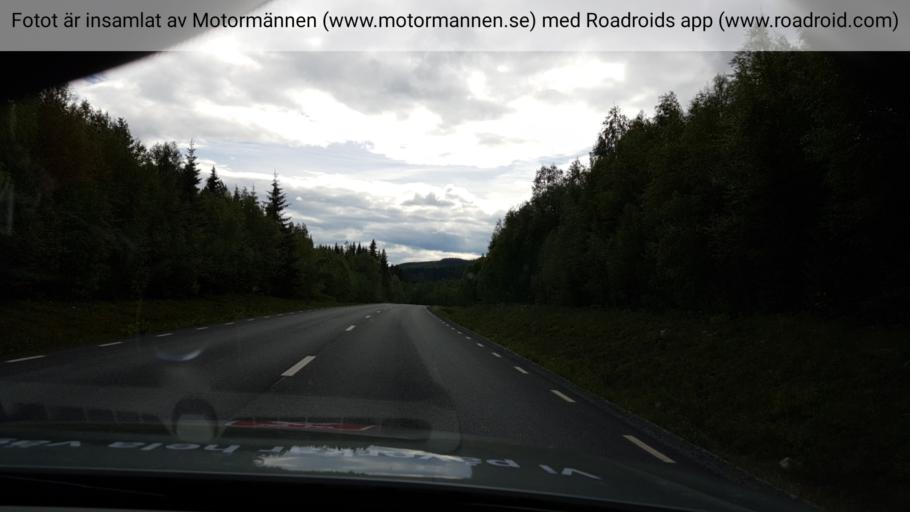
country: SE
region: Jaemtland
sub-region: Stroemsunds Kommun
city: Stroemsund
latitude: 64.1108
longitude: 15.6089
